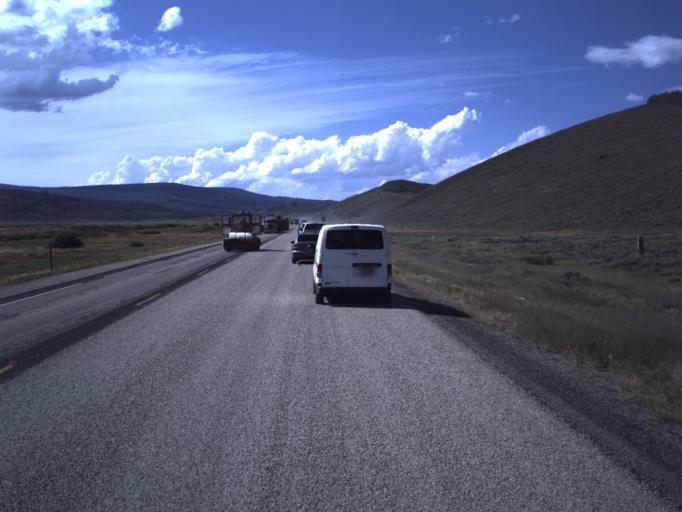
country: US
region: Utah
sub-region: Wasatch County
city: Heber
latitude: 40.2444
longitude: -111.1868
